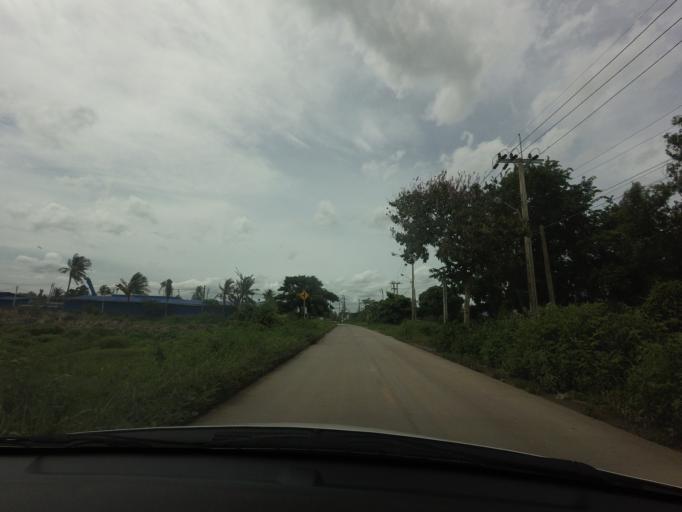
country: TH
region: Bangkok
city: Min Buri
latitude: 13.7901
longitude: 100.7612
